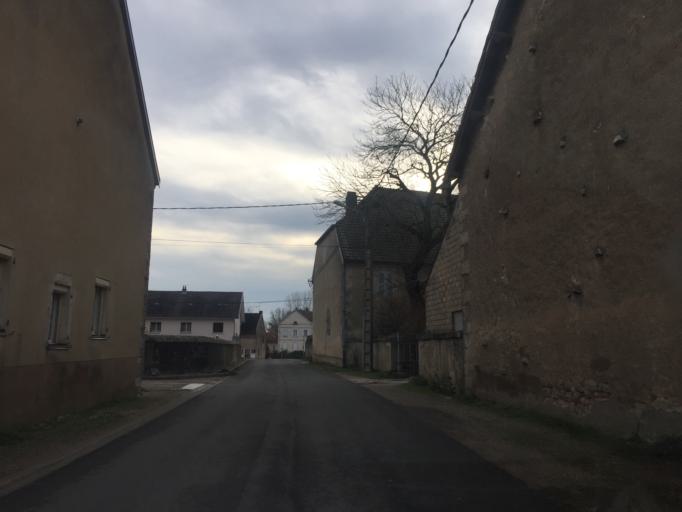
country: FR
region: Franche-Comte
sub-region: Departement du Jura
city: Tavaux
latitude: 47.0199
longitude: 5.4193
